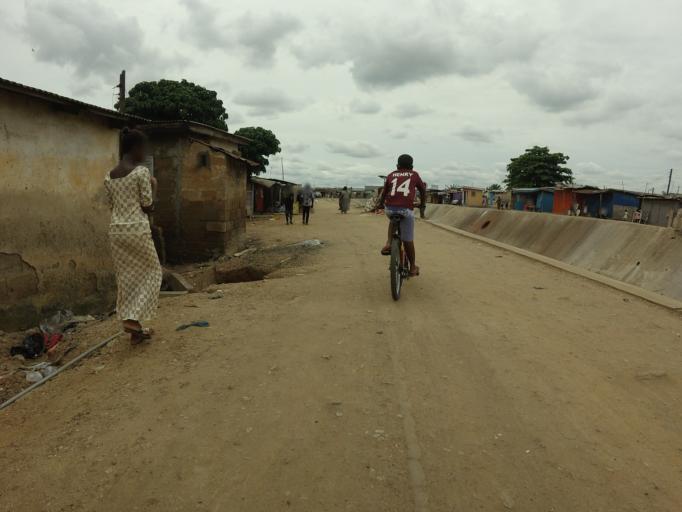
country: GH
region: Greater Accra
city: Accra
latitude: 5.5922
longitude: -0.2140
